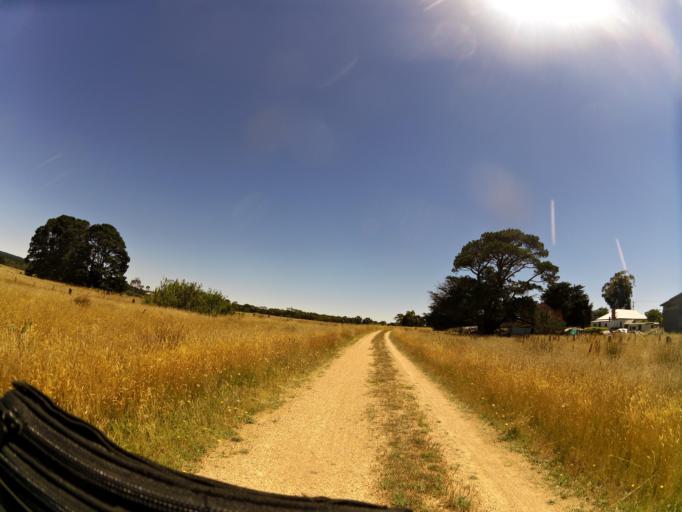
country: AU
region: Victoria
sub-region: Ballarat North
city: Delacombe
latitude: -37.6757
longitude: 143.6535
